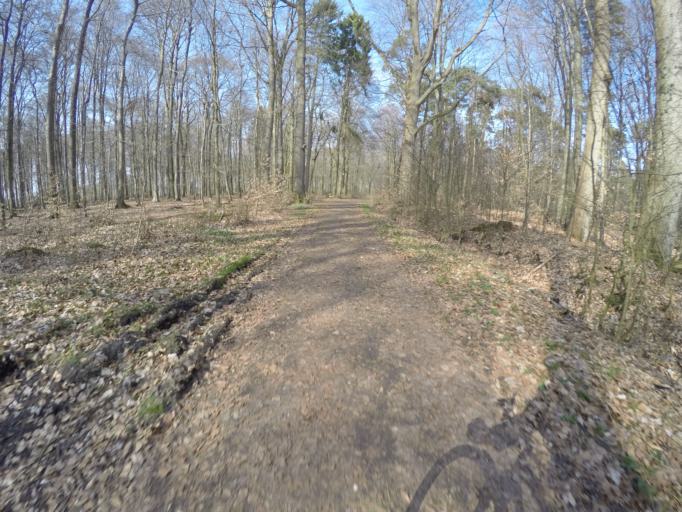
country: DE
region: Schleswig-Holstein
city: Ellerhoop
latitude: 53.7185
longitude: 9.7932
